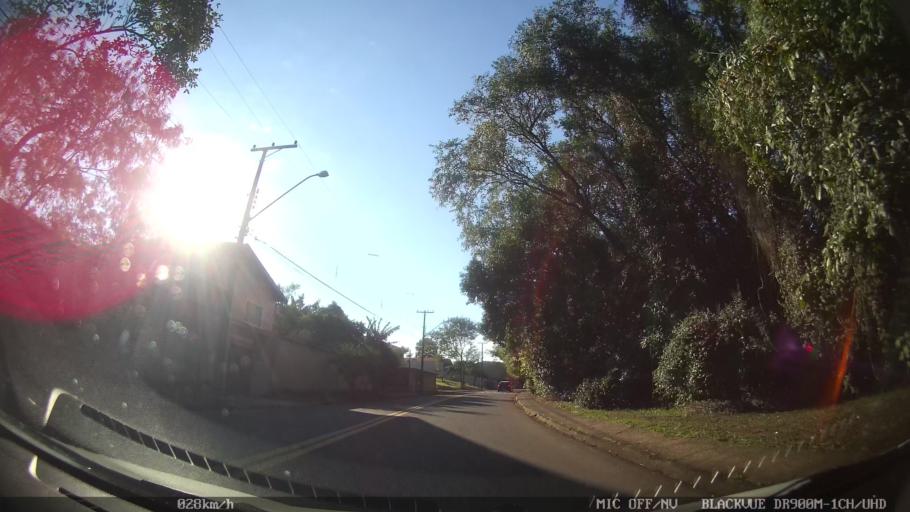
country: BR
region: Sao Paulo
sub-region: Piracicaba
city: Piracicaba
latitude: -22.6844
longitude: -47.6335
